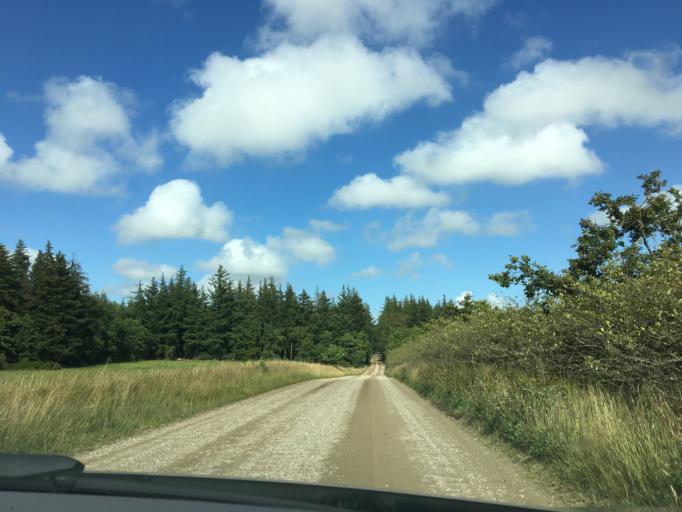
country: DK
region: South Denmark
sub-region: Varde Kommune
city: Oksbol
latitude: 55.7401
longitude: 8.2444
